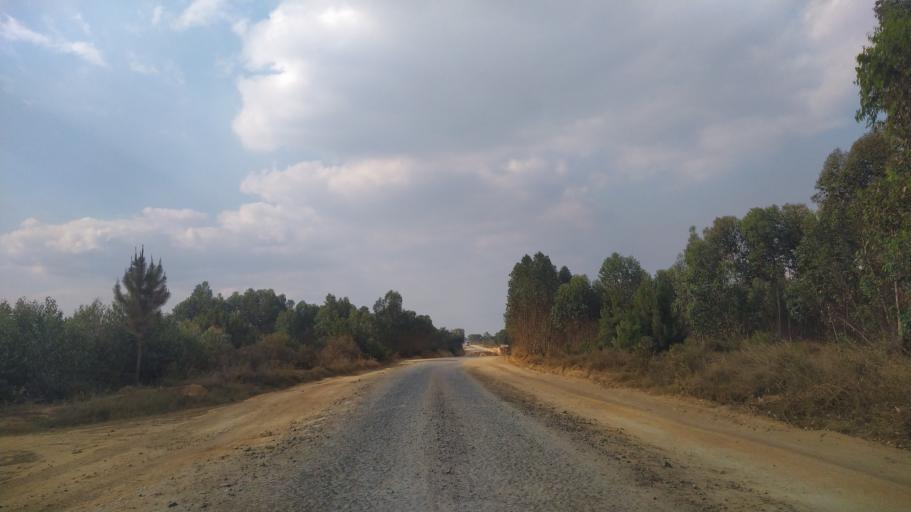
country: MG
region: Alaotra Mangoro
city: Moramanga
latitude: -18.6421
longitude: 48.2755
